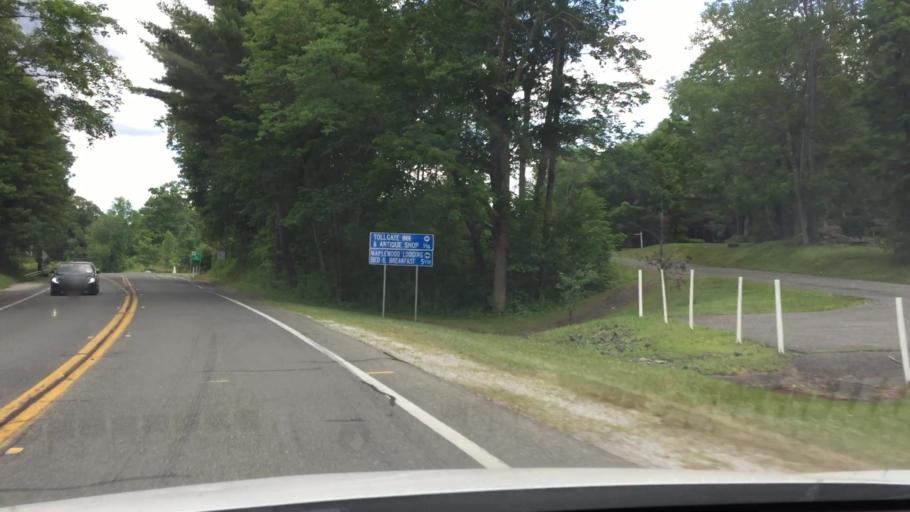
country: US
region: Massachusetts
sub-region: Berkshire County
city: Otis
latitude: 42.2654
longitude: -73.1360
